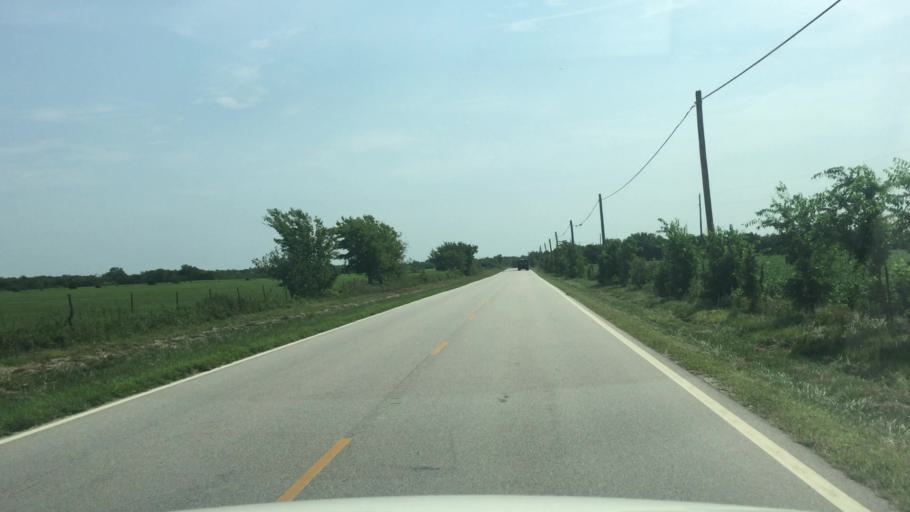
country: US
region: Kansas
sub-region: Labette County
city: Altamont
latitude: 37.1924
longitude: -95.4269
